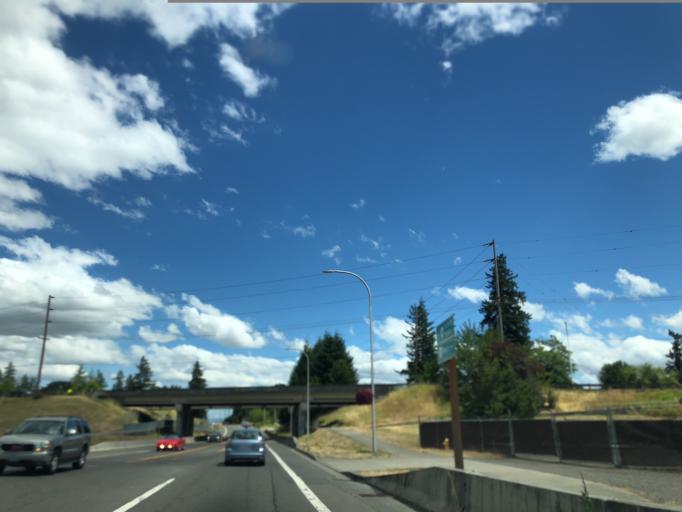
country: US
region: Oregon
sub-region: Marion County
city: Woodburn
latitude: 45.1519
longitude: -122.8465
